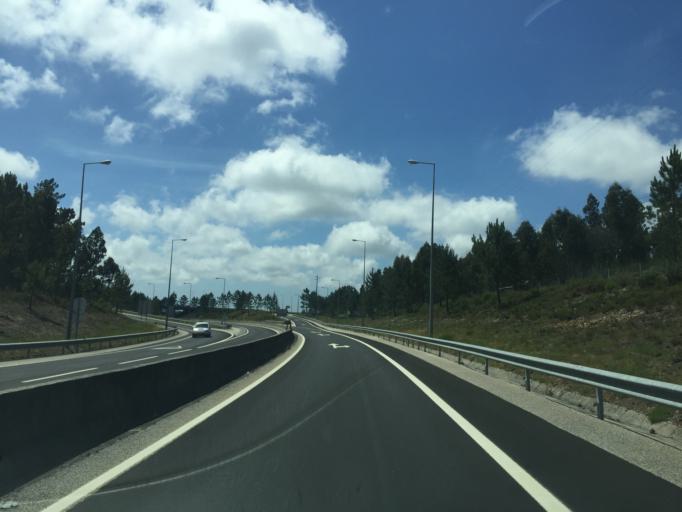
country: PT
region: Leiria
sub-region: Marinha Grande
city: Marinha Grande
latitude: 39.7149
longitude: -8.9203
